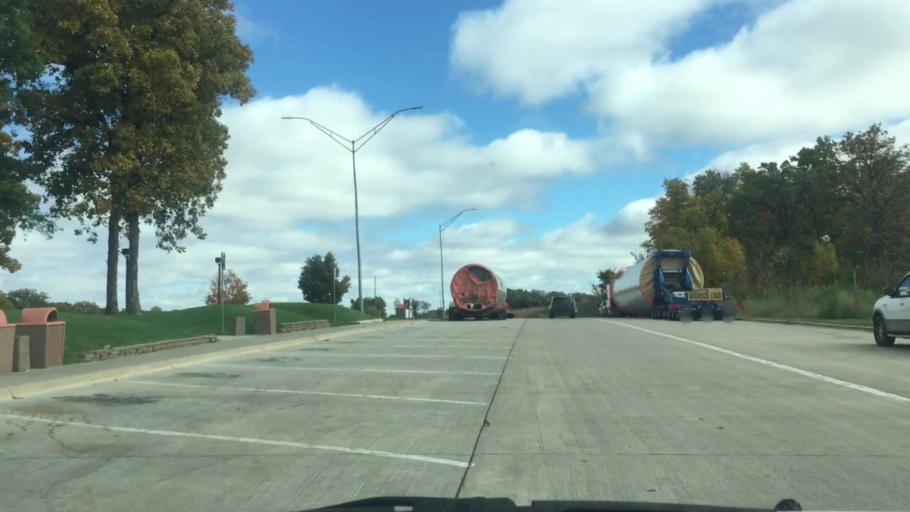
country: US
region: Iowa
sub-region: Poweshiek County
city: Grinnell
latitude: 41.6939
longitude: -92.7735
